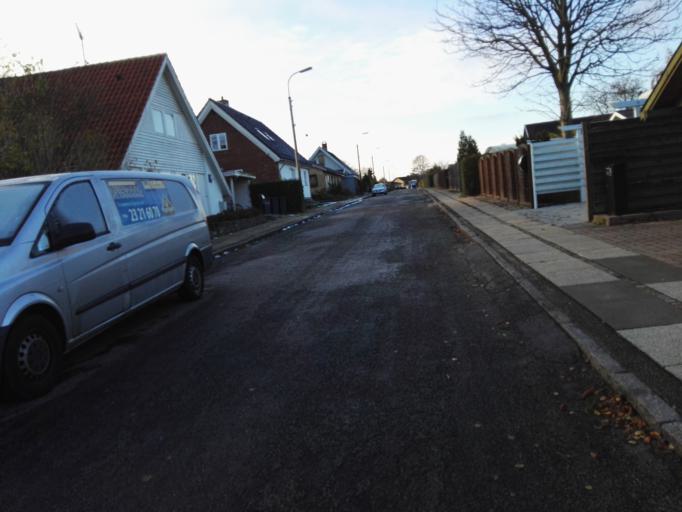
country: DK
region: Capital Region
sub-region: Herlev Kommune
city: Herlev
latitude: 55.7224
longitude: 12.4174
